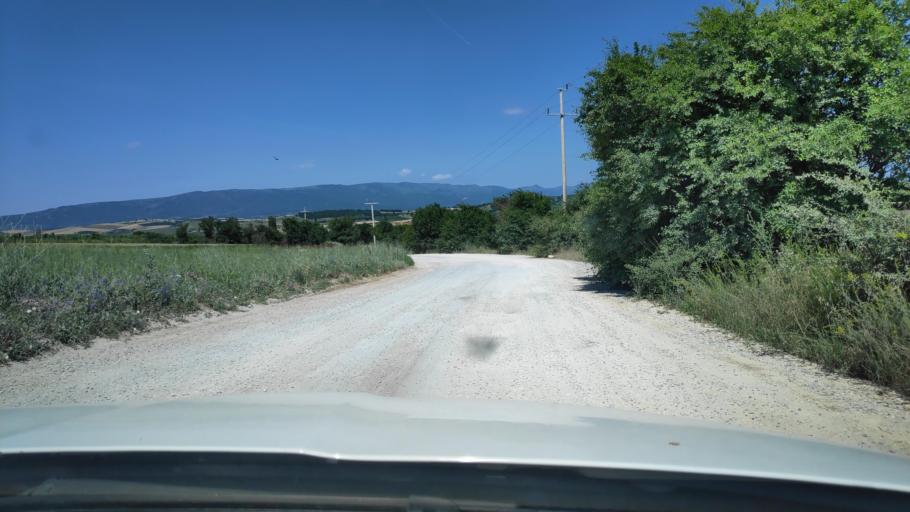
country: MK
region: Kumanovo
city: Romanovce
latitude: 42.0764
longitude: 21.7086
